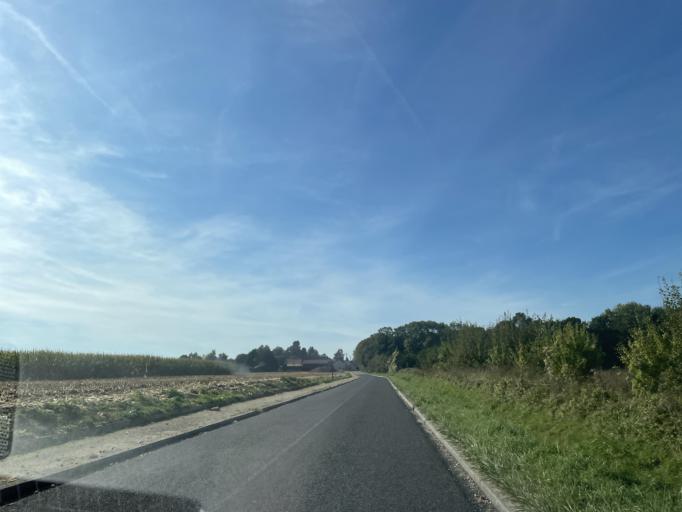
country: FR
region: Ile-de-France
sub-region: Departement de Seine-et-Marne
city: Saint-Jean-les-Deux-Jumeaux
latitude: 48.9468
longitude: 2.9916
